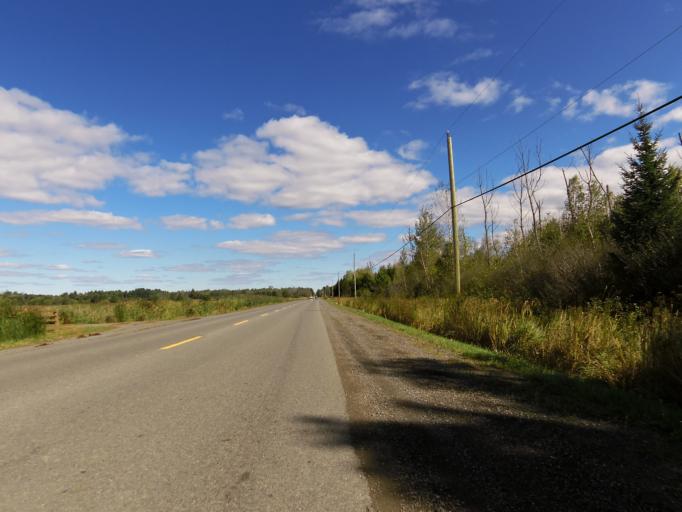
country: CA
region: Ontario
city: Ottawa
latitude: 45.3537
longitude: -75.5494
